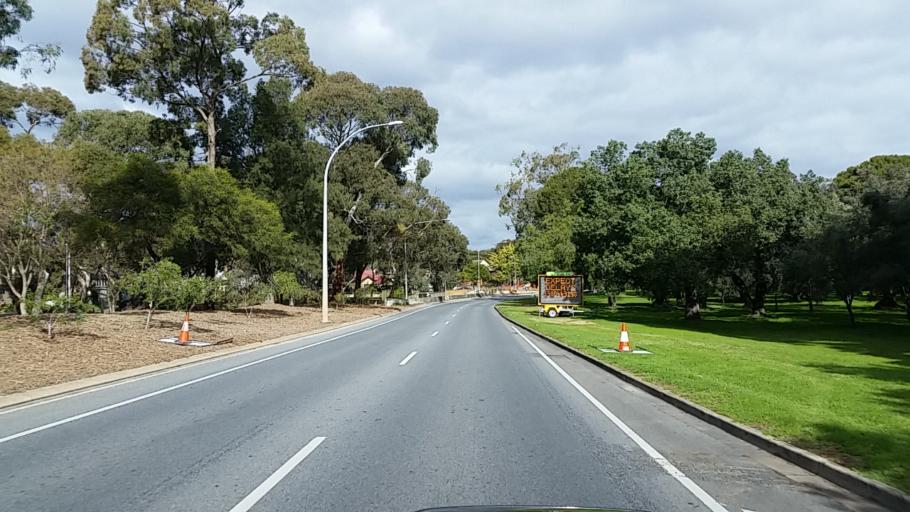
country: AU
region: South Australia
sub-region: Adelaide
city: North Adelaide
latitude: -34.9045
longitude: 138.6120
